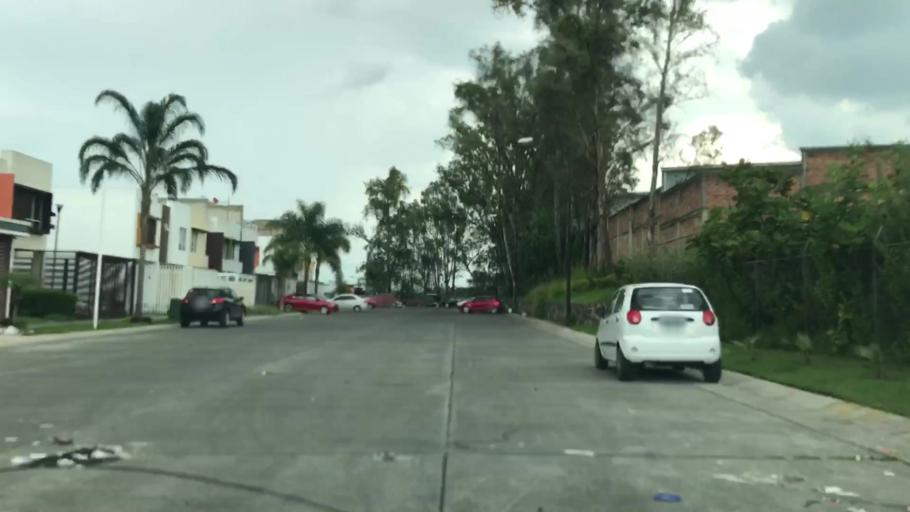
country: MX
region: Jalisco
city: Guadalajara
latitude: 20.6171
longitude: -103.3967
